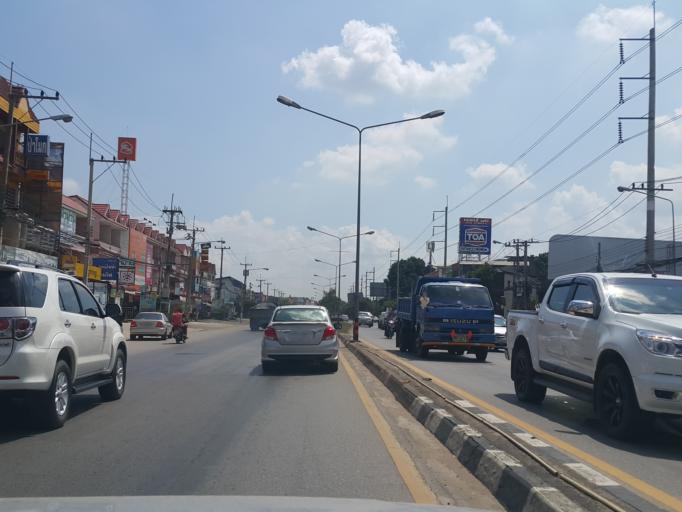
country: TH
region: Chiang Mai
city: San Sai
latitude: 18.8927
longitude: 99.0106
